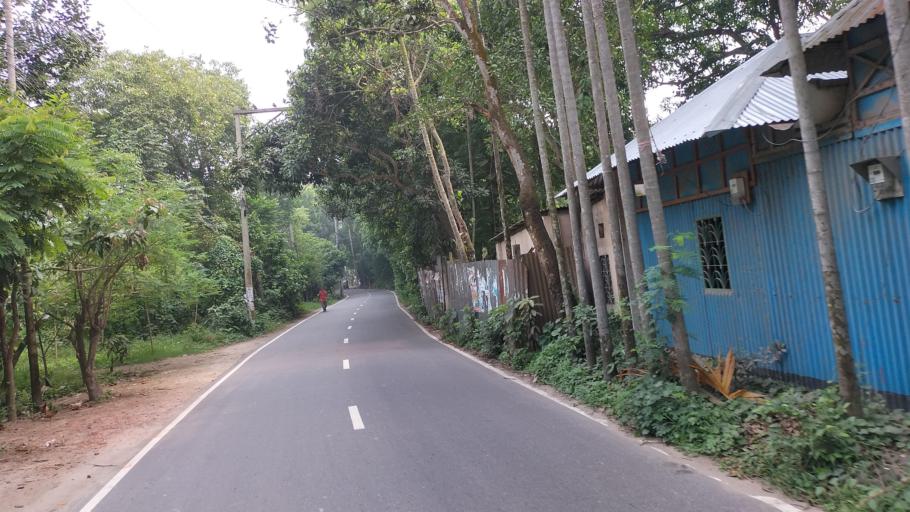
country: BD
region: Dhaka
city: Azimpur
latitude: 23.7002
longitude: 90.2943
